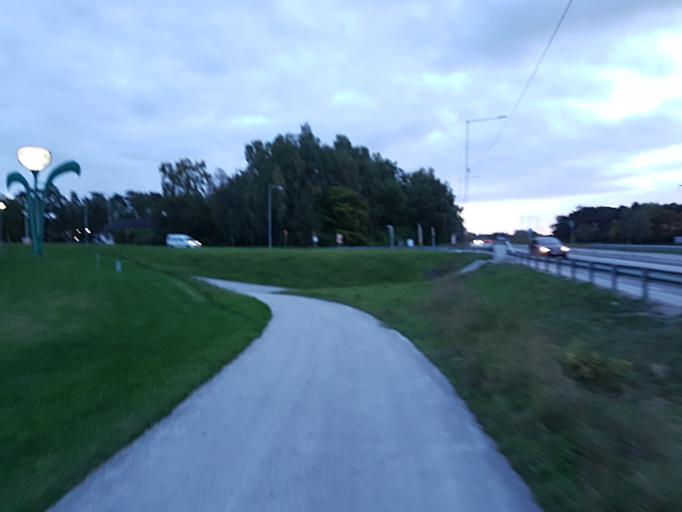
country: SE
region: Gotland
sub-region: Gotland
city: Visby
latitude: 57.6189
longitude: 18.3169
